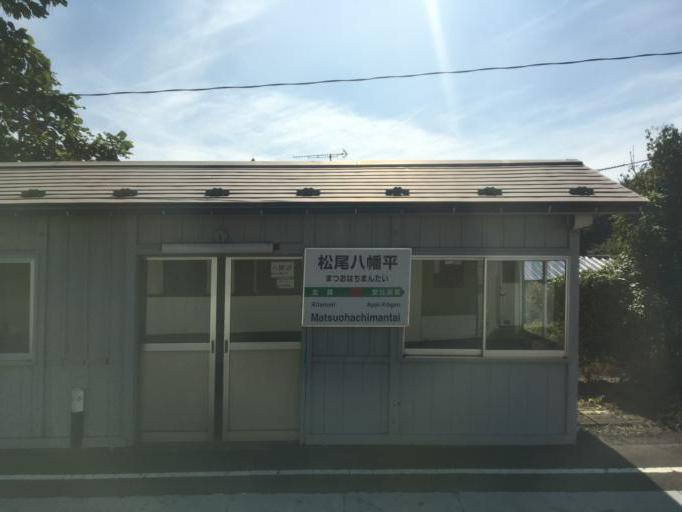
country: JP
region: Iwate
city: Shizukuishi
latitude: 39.9693
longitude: 141.0439
